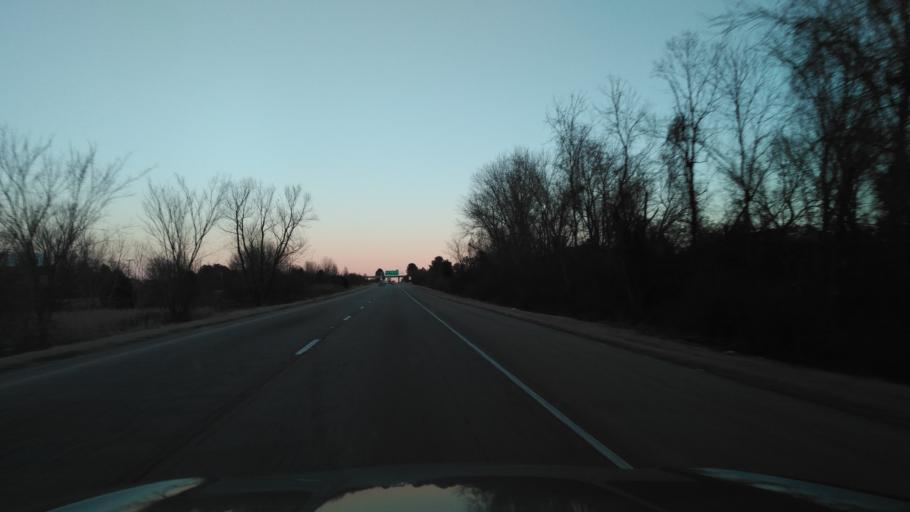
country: US
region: Arkansas
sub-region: Crawford County
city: Van Buren
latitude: 35.4617
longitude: -94.3495
